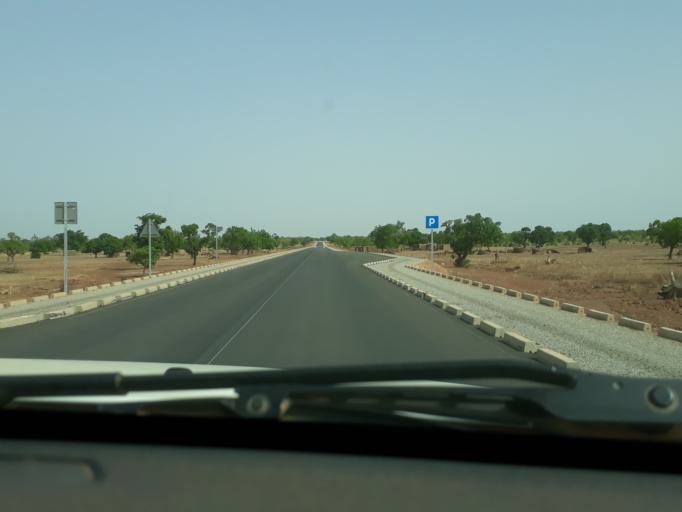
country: BF
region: Plateau-Central
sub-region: Province d'Oubritenga
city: Ziniare
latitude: 12.5650
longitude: -1.4584
